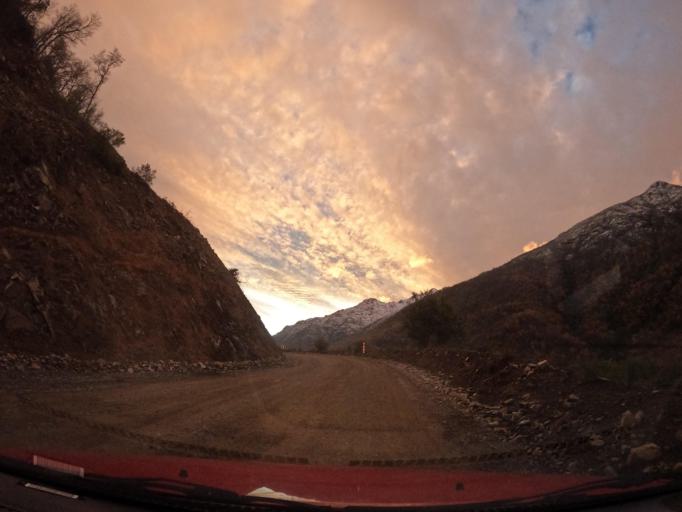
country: CL
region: Maule
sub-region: Provincia de Linares
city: Colbun
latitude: -35.8560
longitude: -71.1687
